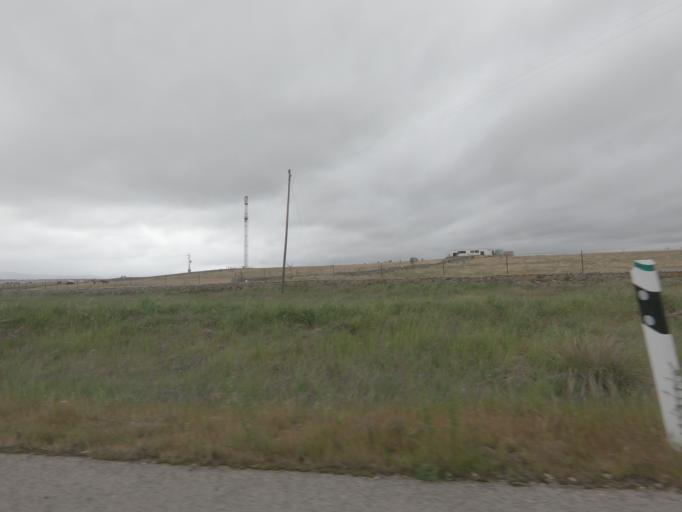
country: ES
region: Extremadura
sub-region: Provincia de Caceres
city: Malpartida de Caceres
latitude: 39.3767
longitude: -6.4506
